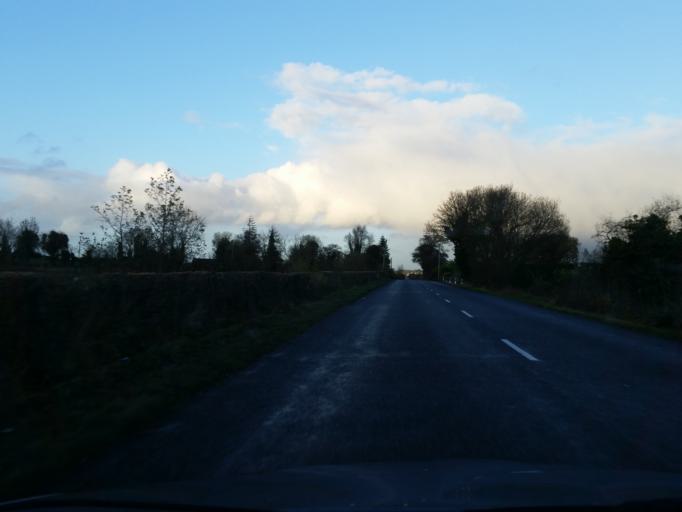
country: GB
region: Northern Ireland
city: Lisnaskea
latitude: 54.2209
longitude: -7.4625
